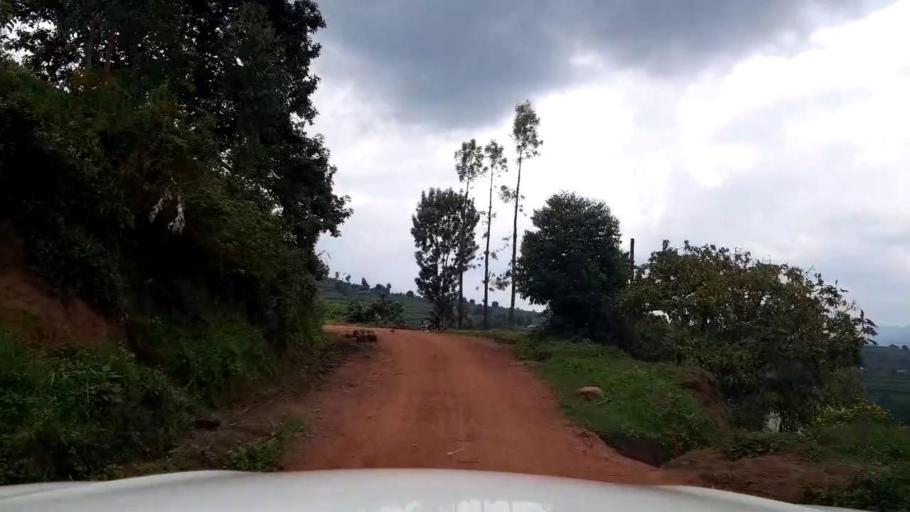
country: RW
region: Northern Province
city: Byumba
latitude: -1.4786
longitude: 29.9020
